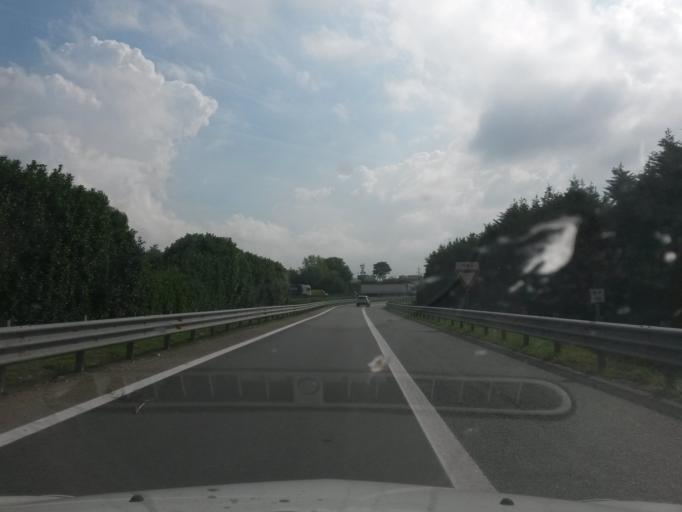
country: IT
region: Piedmont
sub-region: Provincia di Torino
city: Tetti Neirotti
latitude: 45.0629
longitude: 7.5413
